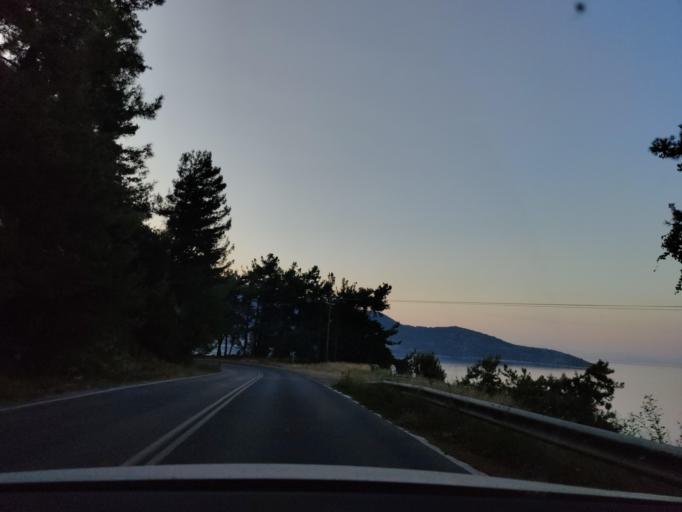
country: GR
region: East Macedonia and Thrace
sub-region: Nomos Kavalas
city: Potamia
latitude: 40.7066
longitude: 24.7667
